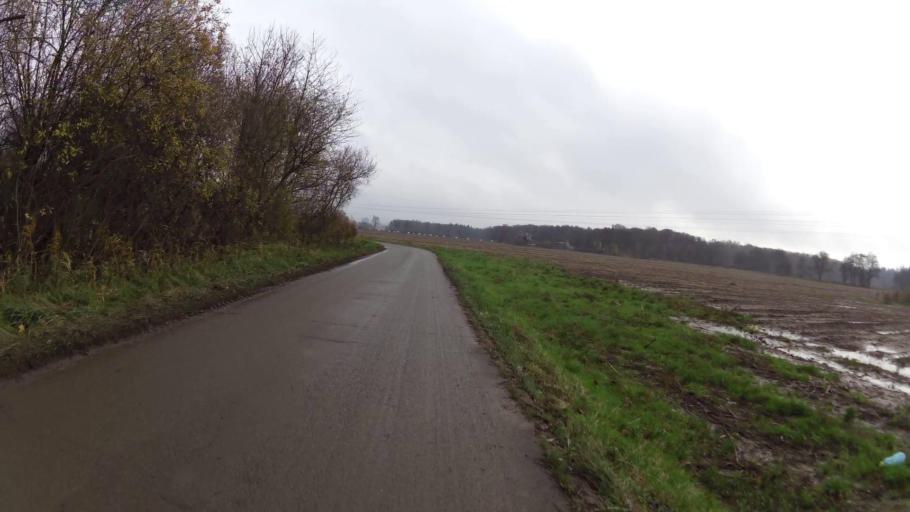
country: PL
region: West Pomeranian Voivodeship
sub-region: Koszalin
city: Koszalin
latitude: 54.2333
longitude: 16.1503
